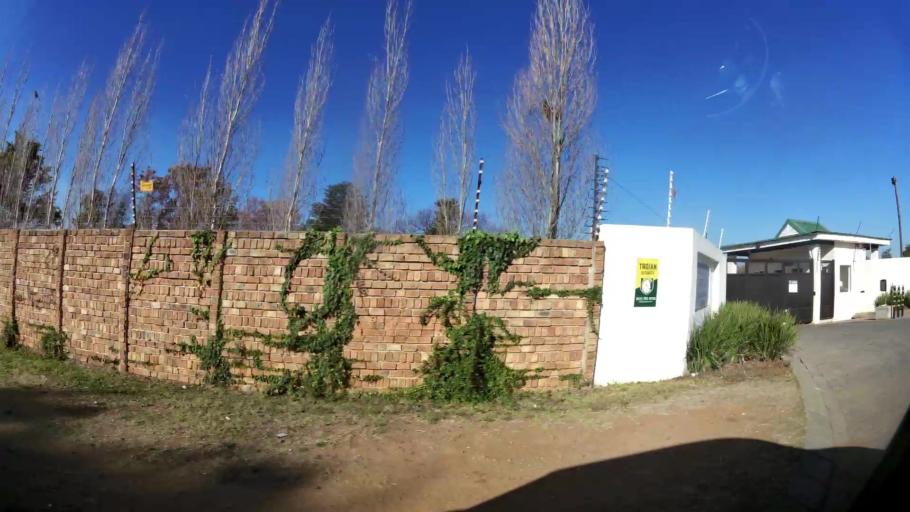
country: ZA
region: Gauteng
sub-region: City of Johannesburg Metropolitan Municipality
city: Roodepoort
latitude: -26.0939
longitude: 27.9458
